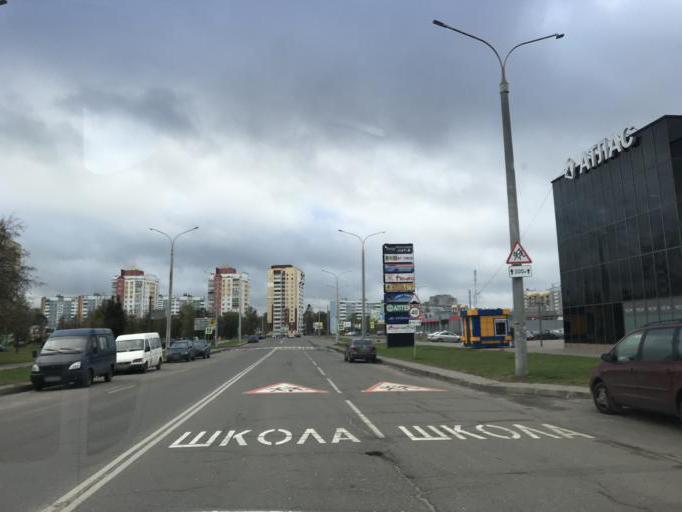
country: BY
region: Mogilev
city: Mahilyow
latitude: 53.8822
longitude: 30.3683
